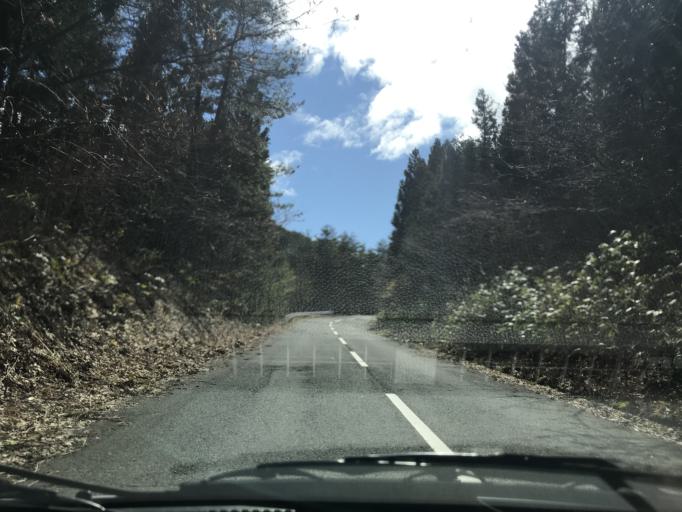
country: JP
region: Iwate
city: Mizusawa
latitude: 39.0701
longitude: 140.9865
